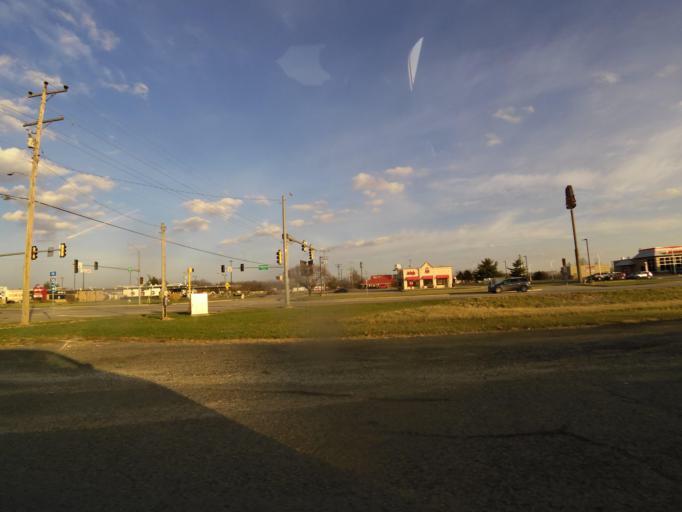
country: US
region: Illinois
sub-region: Fayette County
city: Vandalia
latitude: 38.9769
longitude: -89.1000
